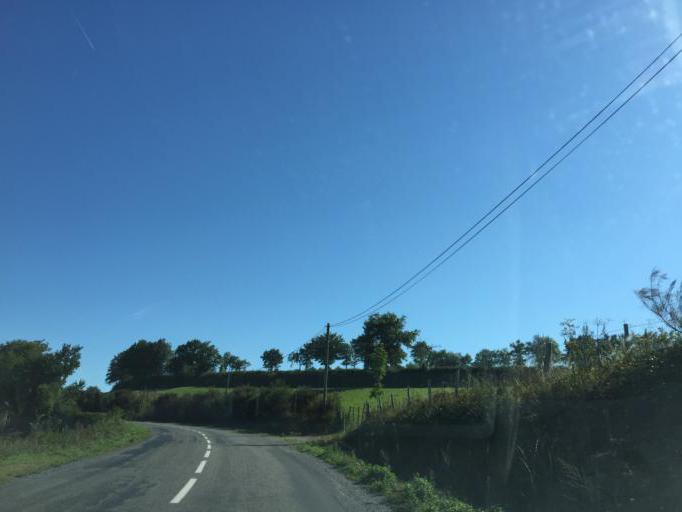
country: FR
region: Midi-Pyrenees
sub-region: Departement de l'Aveyron
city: Pont-de-Salars
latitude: 44.3208
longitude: 2.7557
